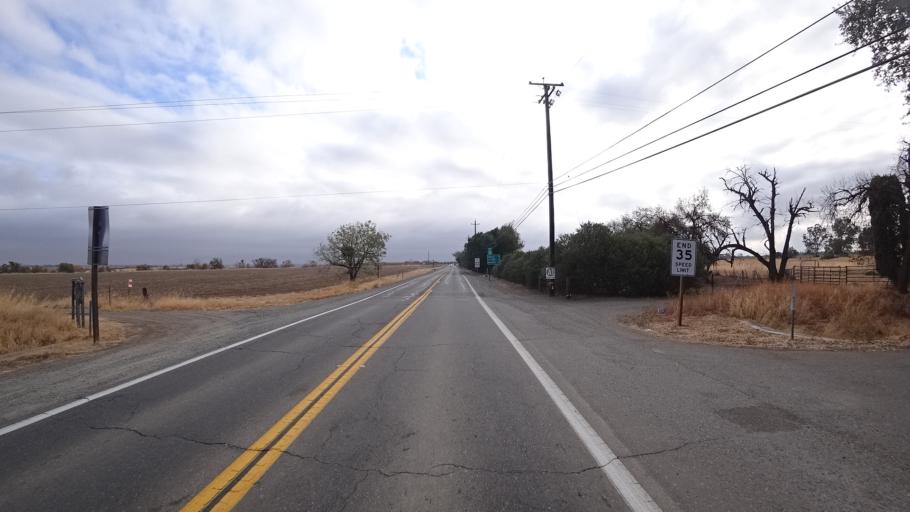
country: US
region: California
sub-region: Yolo County
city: Esparto
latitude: 38.7068
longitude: -122.0461
